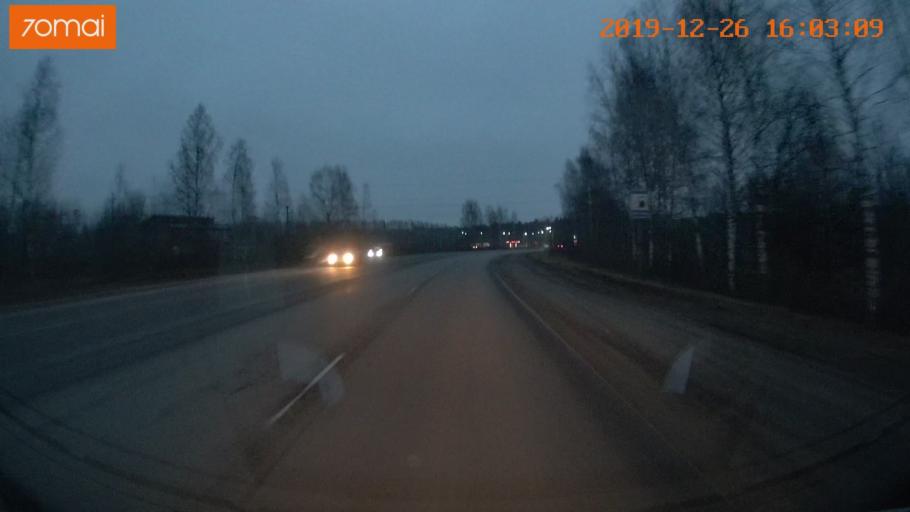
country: RU
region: Jaroslavl
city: Rybinsk
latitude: 58.0114
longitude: 38.8515
